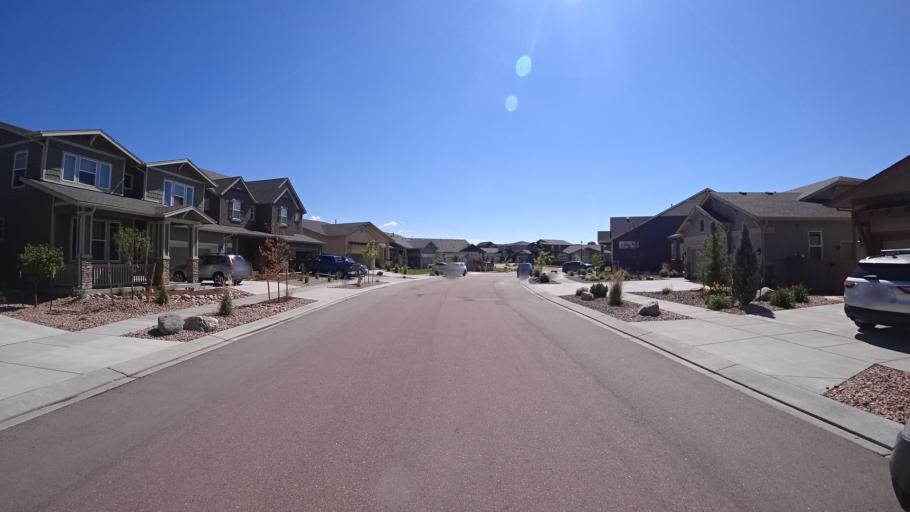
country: US
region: Colorado
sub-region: El Paso County
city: Black Forest
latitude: 38.9787
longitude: -104.7480
